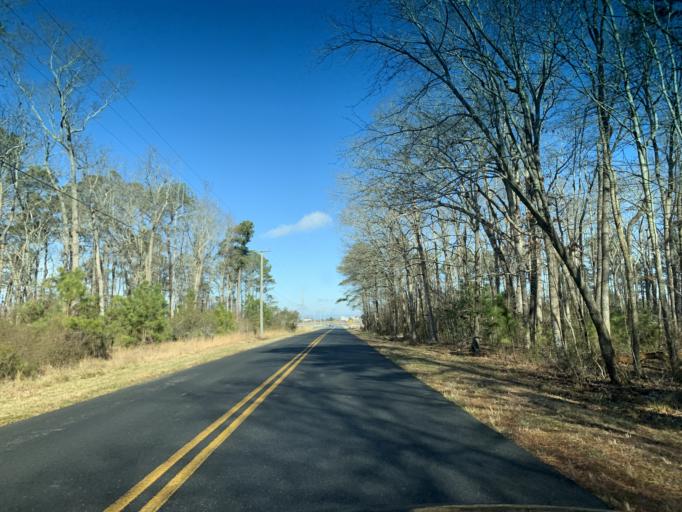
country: US
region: Maryland
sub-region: Worcester County
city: Ocean Pines
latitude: 38.3965
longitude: -75.1093
